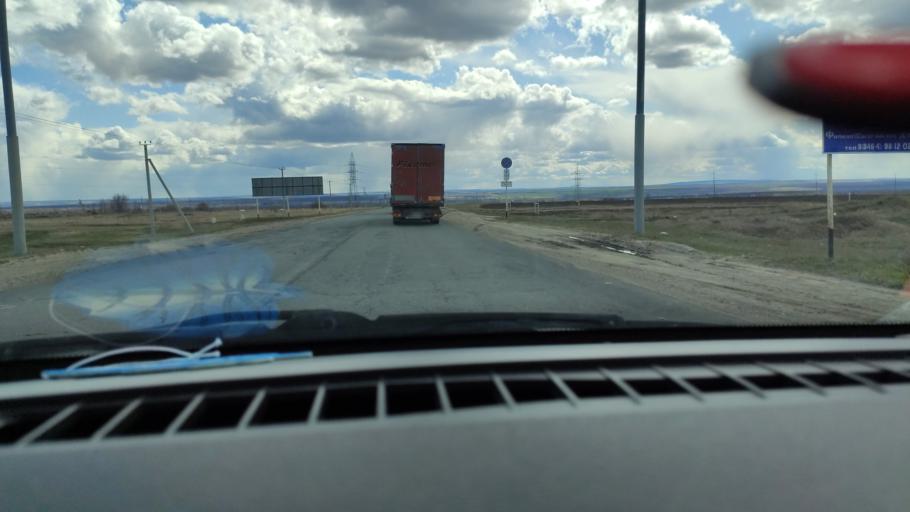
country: RU
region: Samara
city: Varlamovo
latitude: 53.1855
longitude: 48.2903
